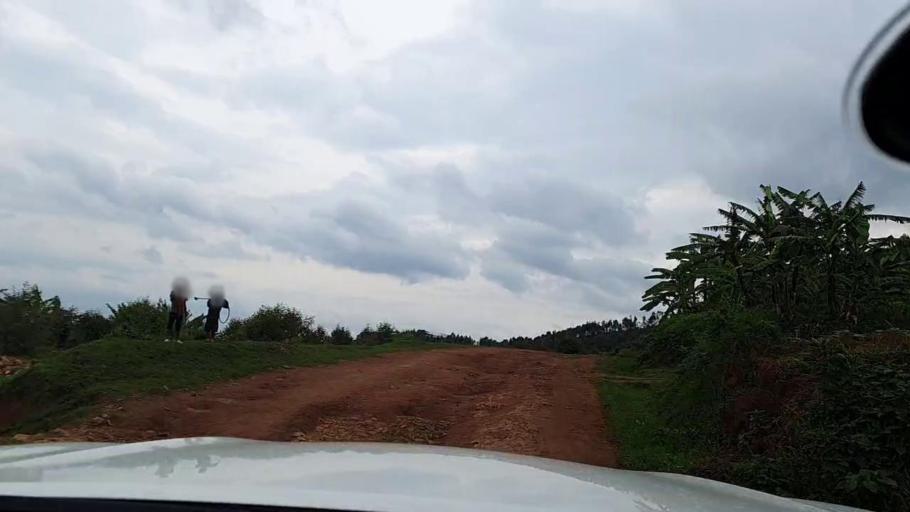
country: RW
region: Western Province
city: Kibuye
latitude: -2.1899
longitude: 29.2995
